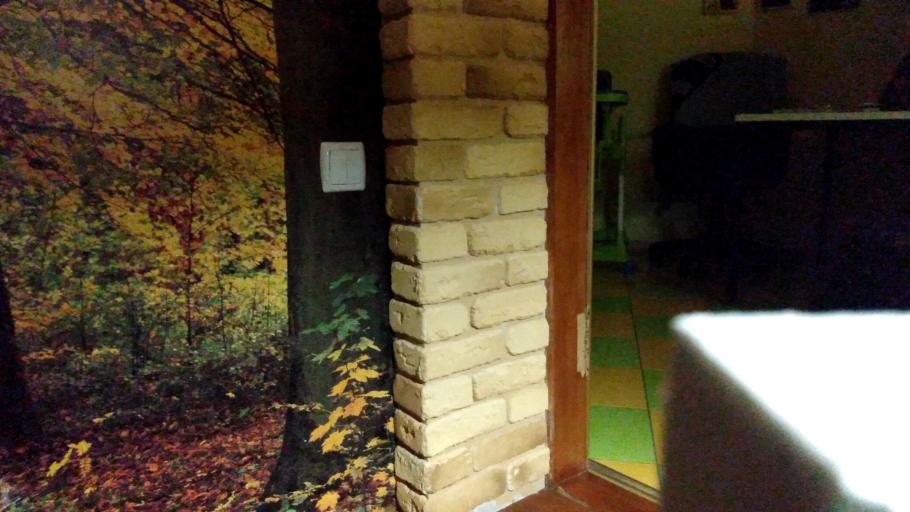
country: RU
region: Vologda
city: Lipin Bor
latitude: 60.9464
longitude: 37.9802
